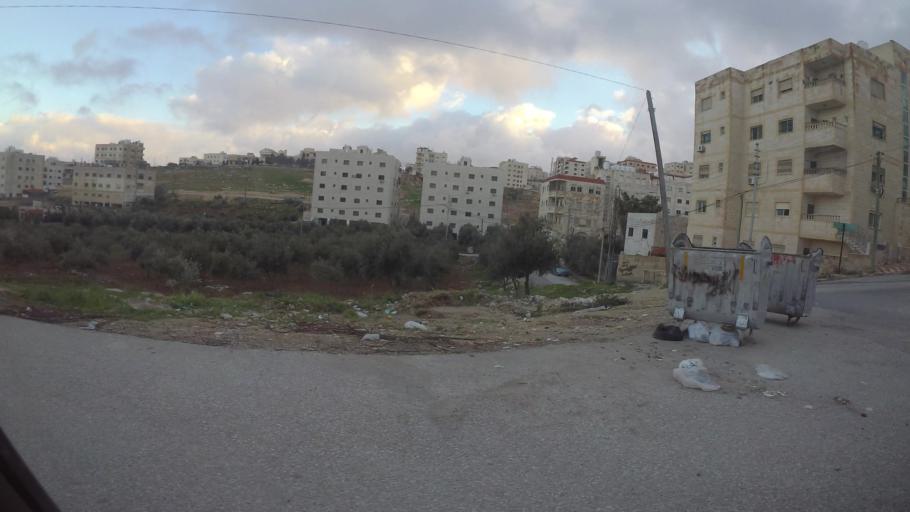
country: JO
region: Amman
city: Al Jubayhah
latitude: 32.0526
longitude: 35.8956
